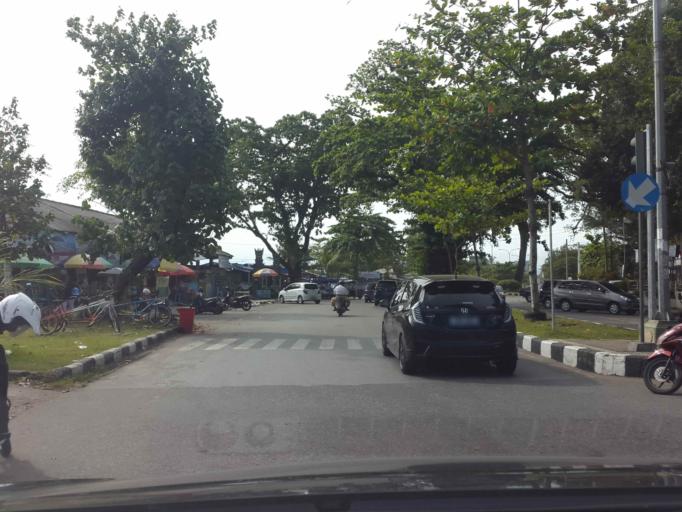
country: ID
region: West Sumatra
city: Padang
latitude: -0.9603
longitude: 100.3535
